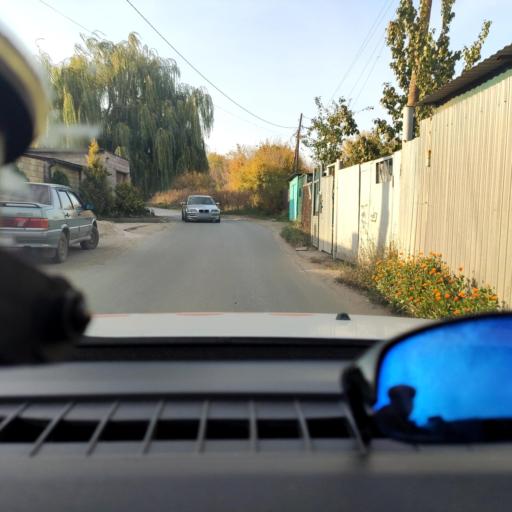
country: RU
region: Samara
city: Samara
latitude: 53.2336
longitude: 50.2340
